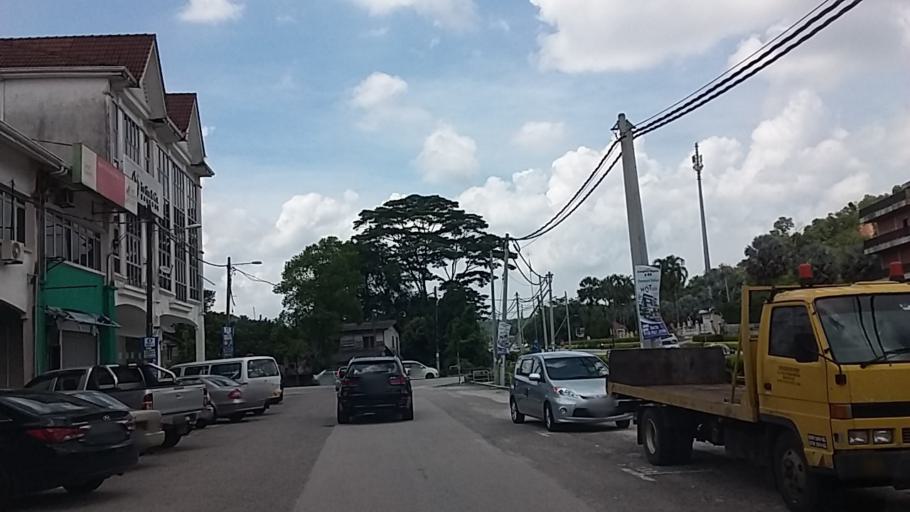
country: MY
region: Johor
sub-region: Daerah Batu Pahat
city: Batu Pahat
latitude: 1.8354
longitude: 102.9489
